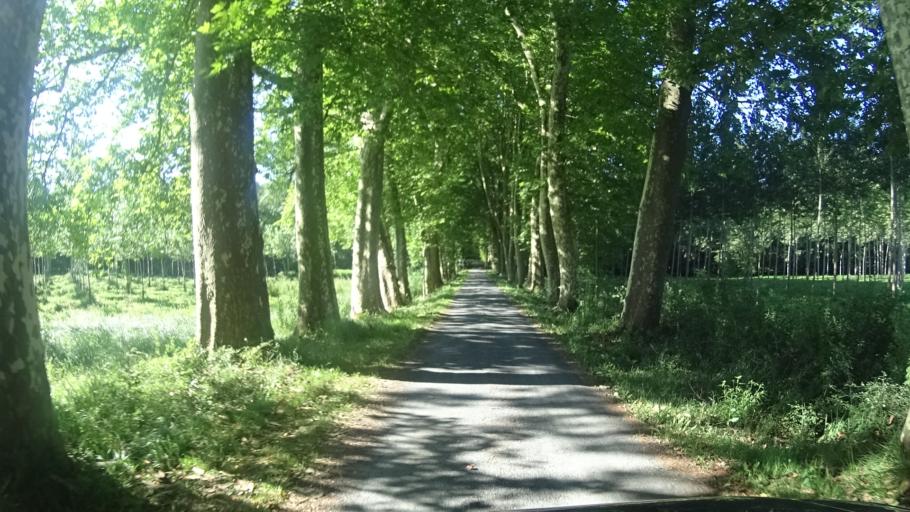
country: FR
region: Aquitaine
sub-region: Departement de la Dordogne
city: Sourzac
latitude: 45.0163
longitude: 0.4388
